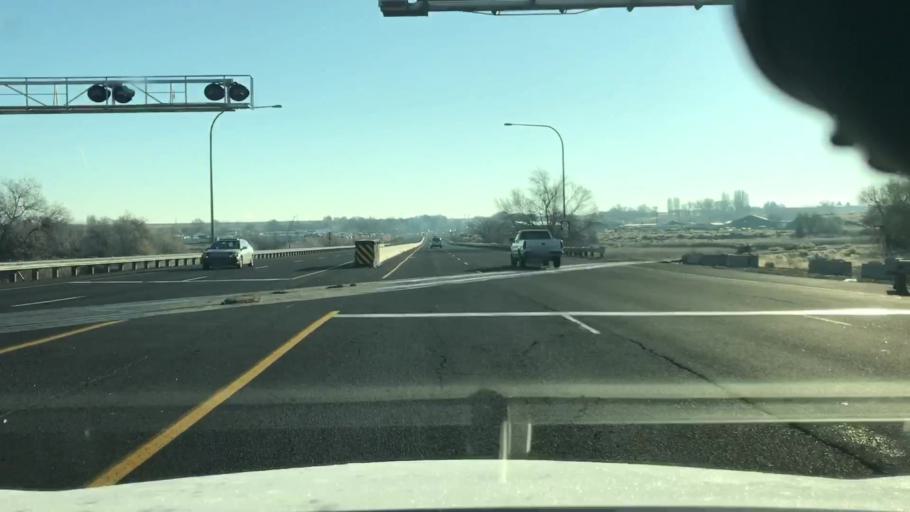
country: US
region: Washington
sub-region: Grant County
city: Moses Lake
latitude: 47.1424
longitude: -119.2718
